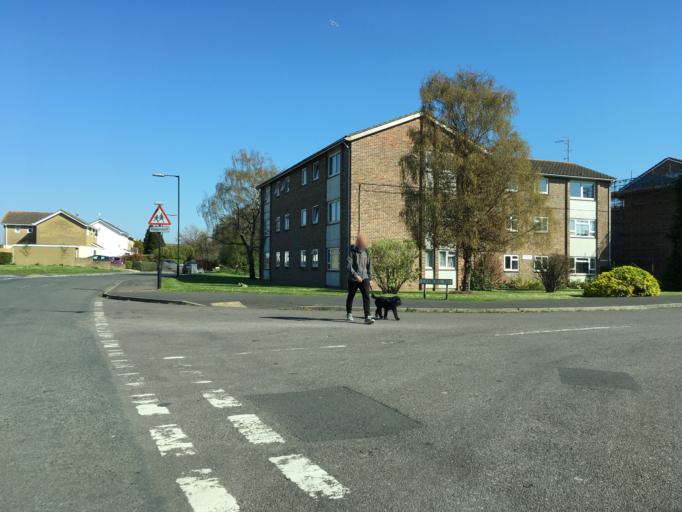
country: GB
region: England
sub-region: North Somerset
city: Portishead
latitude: 51.4782
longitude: -2.7641
